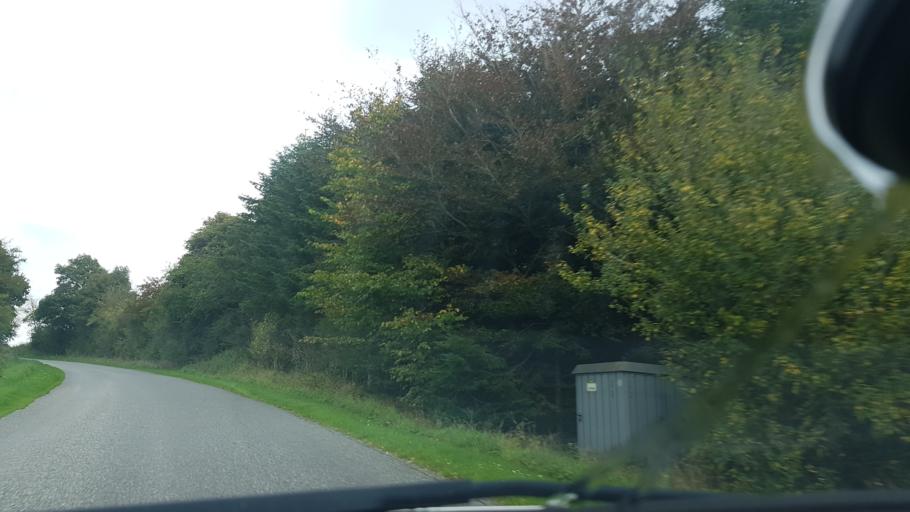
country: DK
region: South Denmark
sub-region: Kolding Kommune
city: Kolding
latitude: 55.5383
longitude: 9.3865
